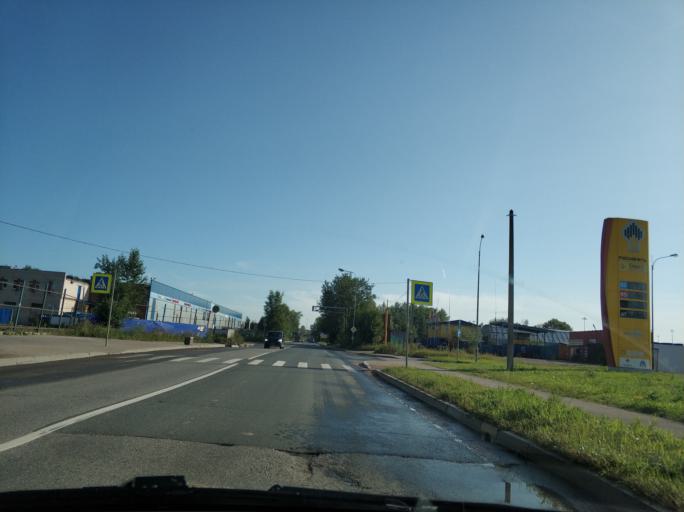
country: RU
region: Leningrad
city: Bugry
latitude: 60.0560
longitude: 30.3822
